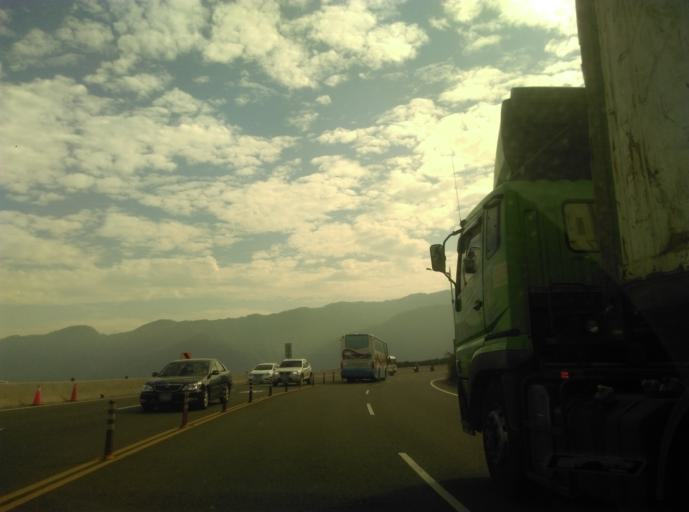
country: TW
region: Taiwan
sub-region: Keelung
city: Keelung
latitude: 25.1742
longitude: 121.7082
